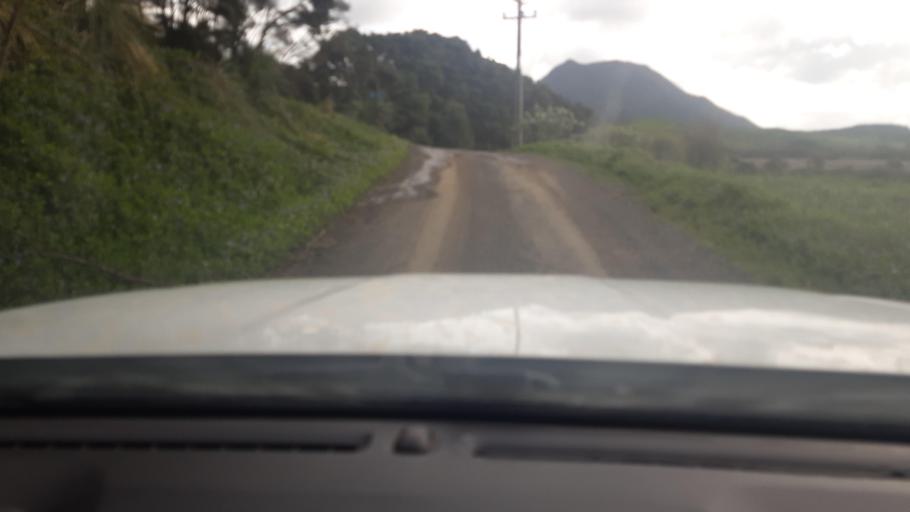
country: NZ
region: Northland
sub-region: Far North District
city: Ahipara
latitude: -35.2600
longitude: 173.2005
